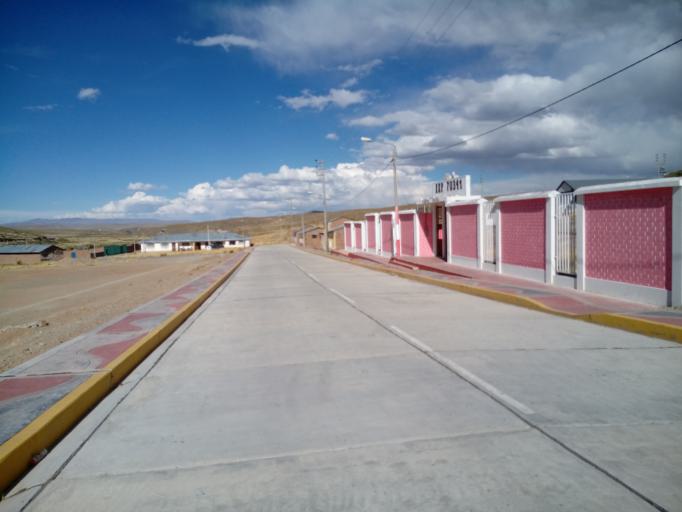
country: PE
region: Puno
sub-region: El Collao
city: Mazo Cruz
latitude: -16.7616
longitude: -69.8539
